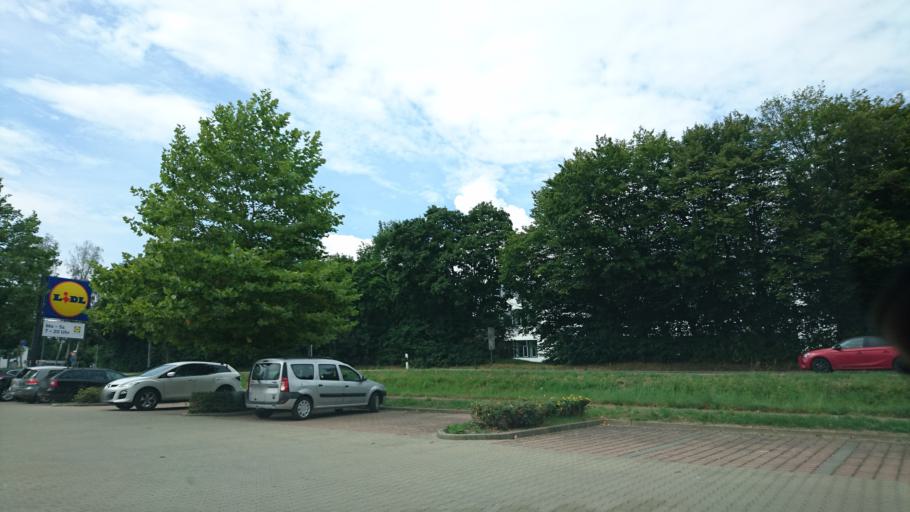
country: DE
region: Bavaria
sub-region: Swabia
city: Dinkelscherben
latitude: 48.3491
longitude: 10.5997
